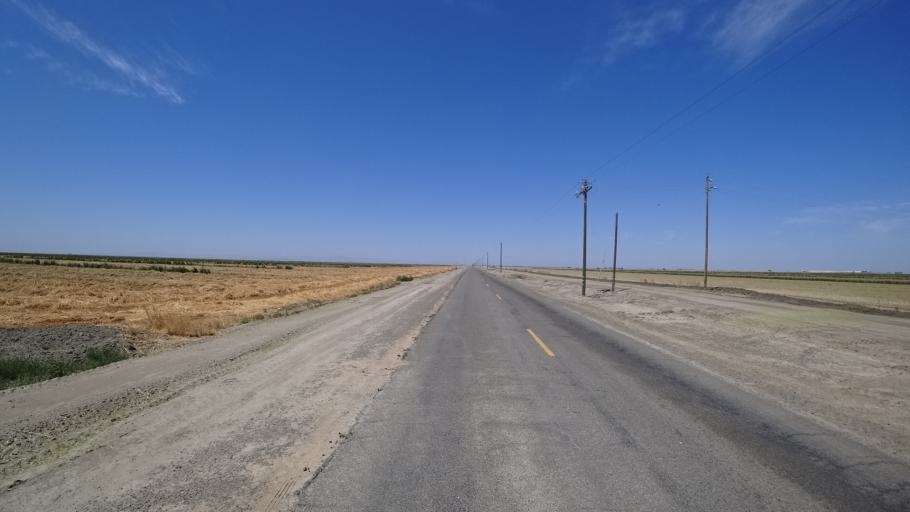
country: US
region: California
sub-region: Kings County
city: Corcoran
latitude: 36.1379
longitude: -119.6678
